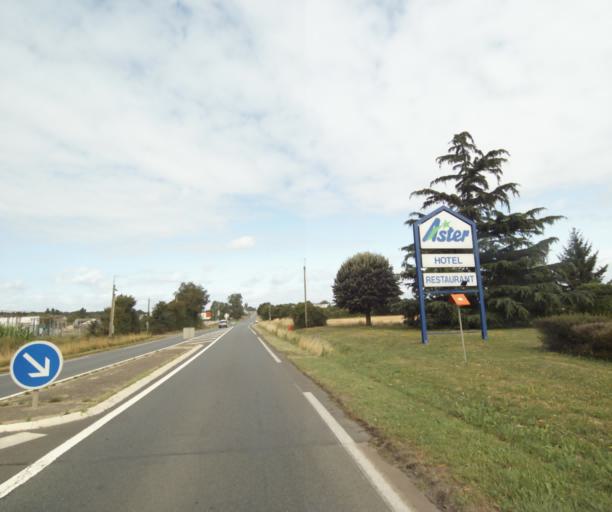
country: FR
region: Pays de la Loire
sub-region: Departement de la Sarthe
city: Solesmes
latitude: 47.8211
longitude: -0.2981
